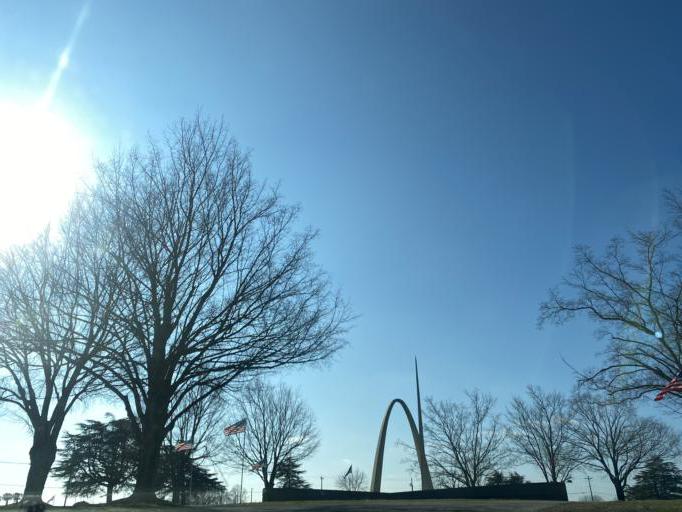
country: US
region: South Carolina
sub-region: Cherokee County
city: Gaffney
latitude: 35.1065
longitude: -81.6948
